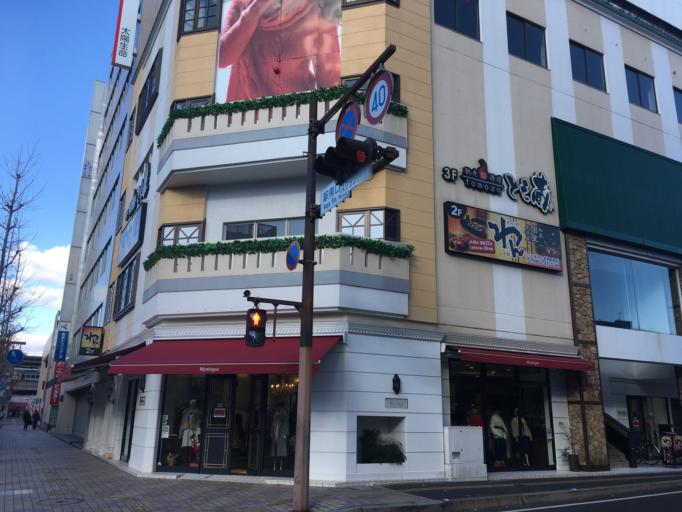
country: JP
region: Saga Prefecture
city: Saga-shi
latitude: 33.2629
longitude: 130.2983
